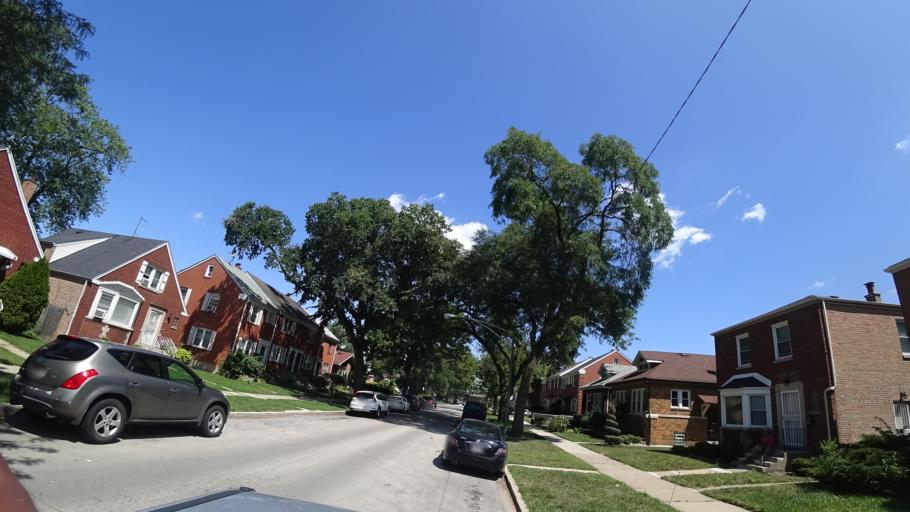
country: US
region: Indiana
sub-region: Lake County
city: Whiting
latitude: 41.7418
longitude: -87.5782
